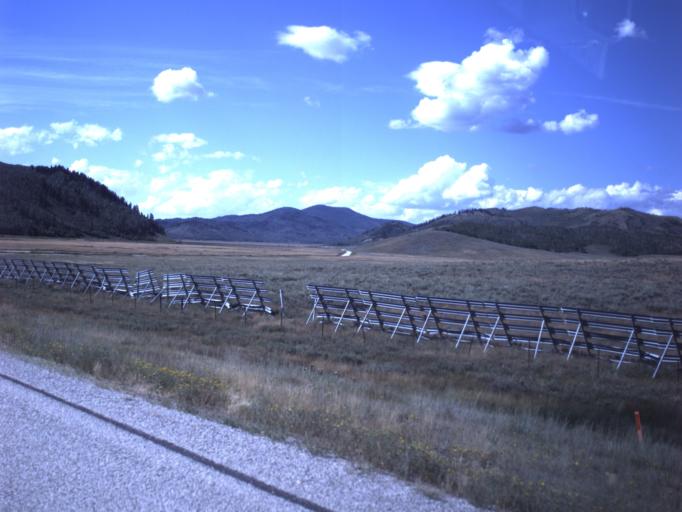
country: US
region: Utah
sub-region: Wasatch County
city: Heber
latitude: 40.2777
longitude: -111.2169
